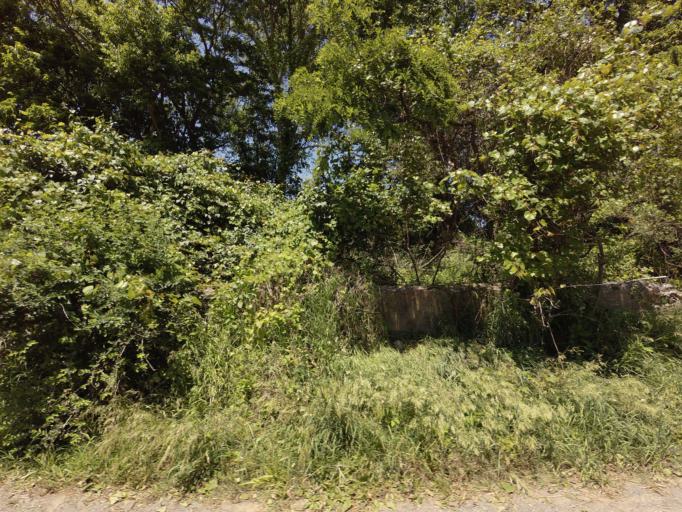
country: US
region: West Virginia
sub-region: Jefferson County
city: Bolivar
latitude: 39.3143
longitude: -77.7731
